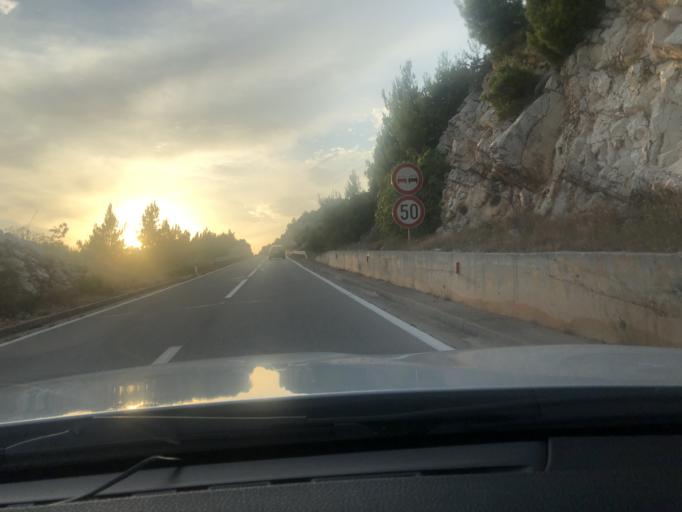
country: HR
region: Splitsko-Dalmatinska
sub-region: Grad Hvar
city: Hvar
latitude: 43.1504
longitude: 16.5193
